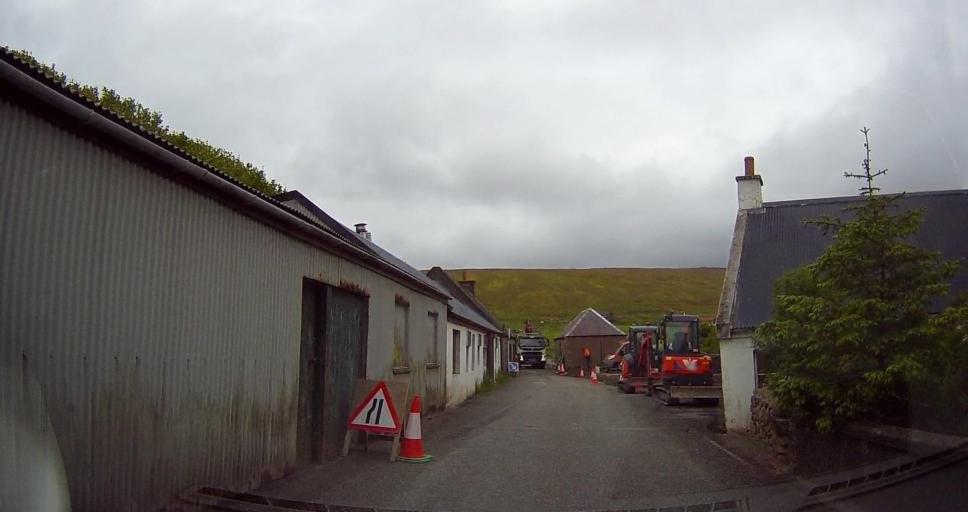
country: GB
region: Scotland
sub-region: Shetland Islands
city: Lerwick
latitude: 60.3504
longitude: -1.2654
